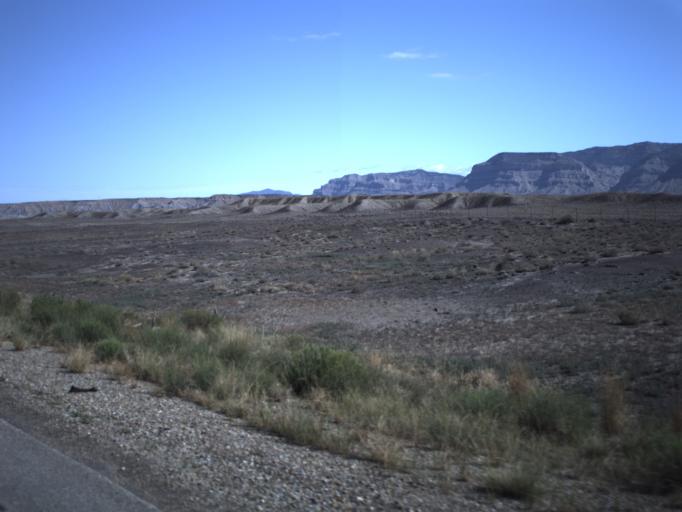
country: US
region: Utah
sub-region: Carbon County
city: East Carbon City
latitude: 39.3510
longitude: -110.3803
